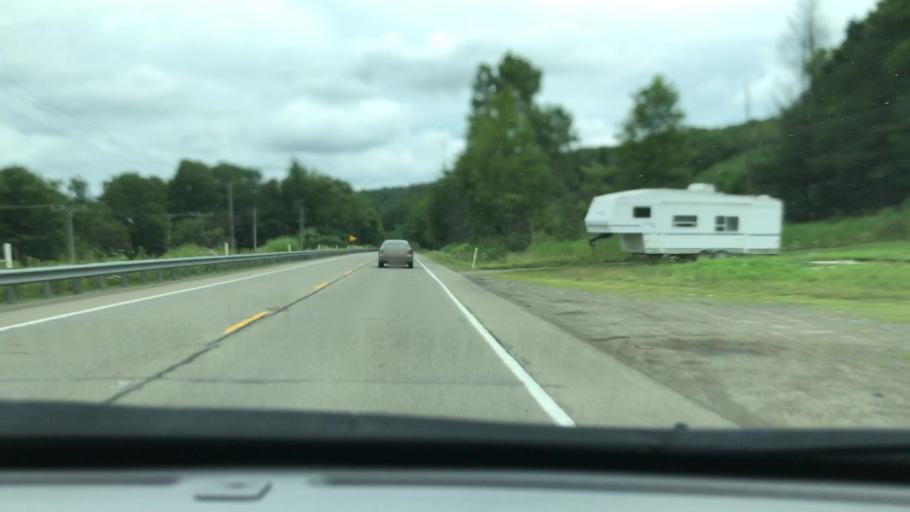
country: US
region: Pennsylvania
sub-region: Elk County
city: Johnsonburg
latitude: 41.5521
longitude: -78.6831
